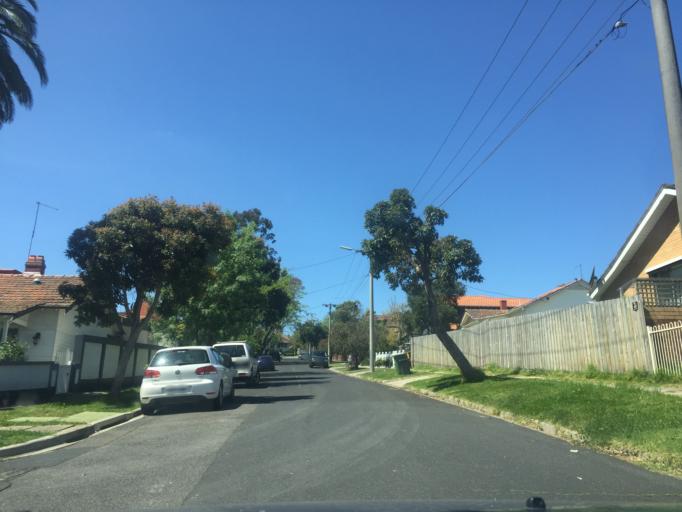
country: AU
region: Victoria
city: Ivanhoe East
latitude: -37.7694
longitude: 145.0528
